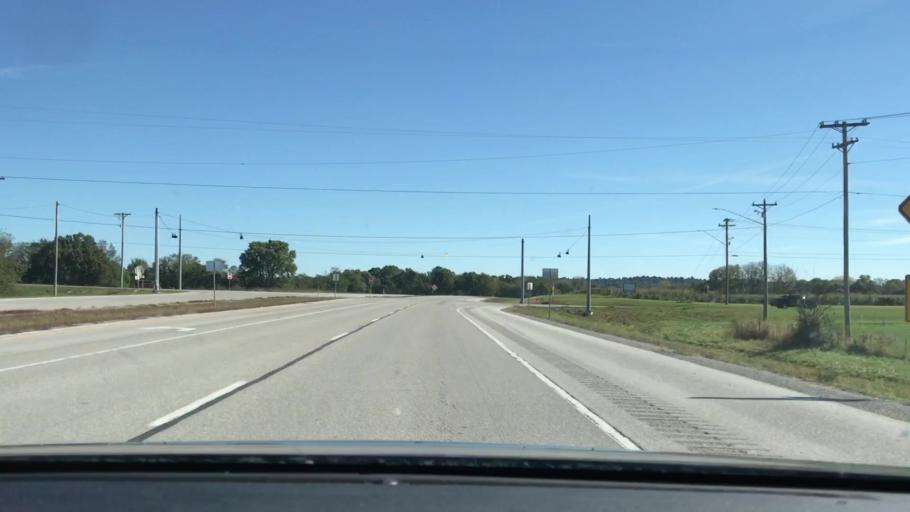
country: US
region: Kentucky
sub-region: Todd County
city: Elkton
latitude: 36.8238
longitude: -87.1616
